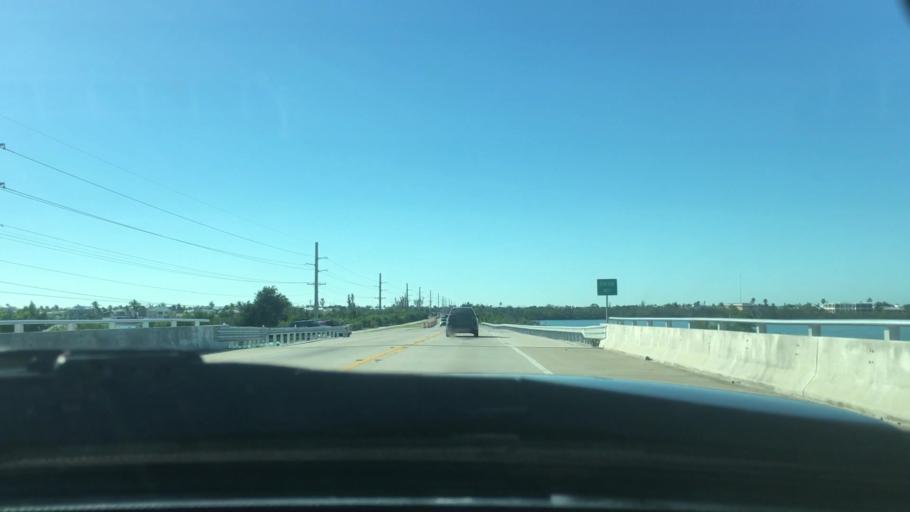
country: US
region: Florida
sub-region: Monroe County
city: Cudjoe Key
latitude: 24.6626
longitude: -81.4678
